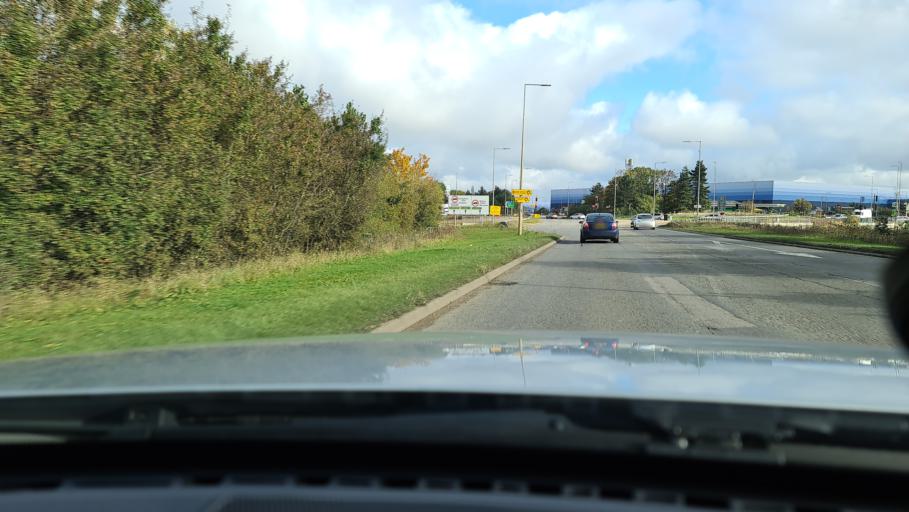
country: GB
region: England
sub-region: Milton Keynes
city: Wavendon
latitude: 52.0315
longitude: -0.6801
